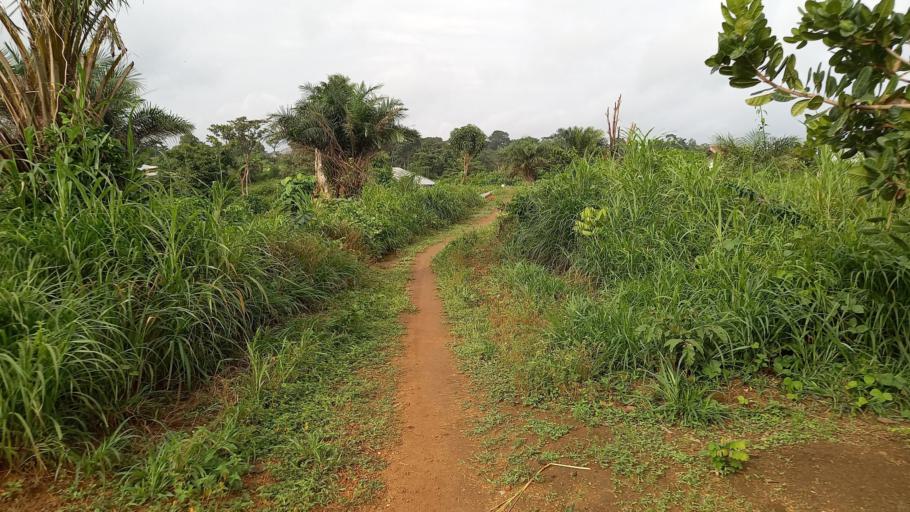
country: SL
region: Eastern Province
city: Kailahun
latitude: 8.2717
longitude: -10.5836
